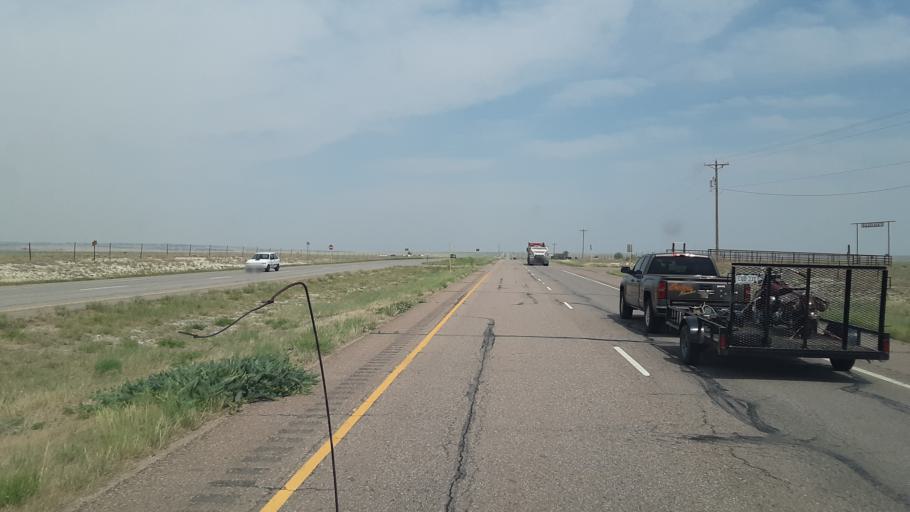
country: US
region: Colorado
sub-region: Fremont County
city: Penrose
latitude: 38.3695
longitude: -104.9263
